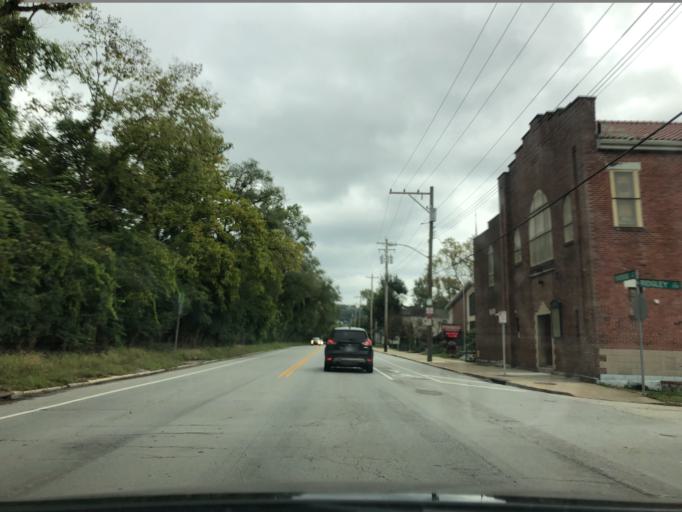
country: US
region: Kentucky
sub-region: Campbell County
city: Dayton
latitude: 39.1201
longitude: -84.4470
